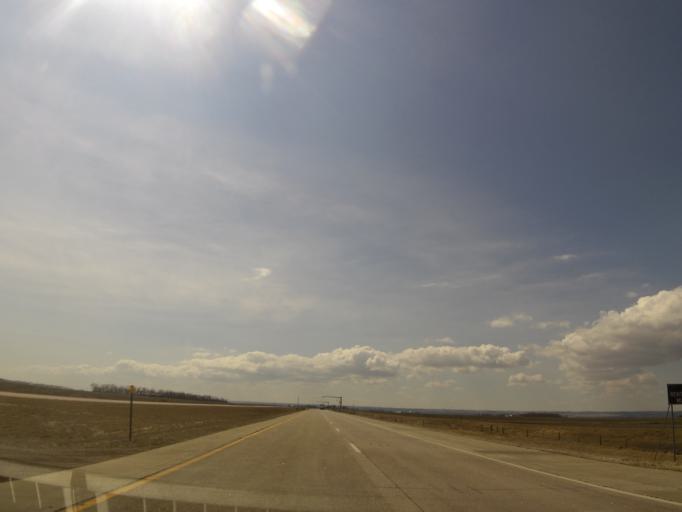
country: US
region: South Dakota
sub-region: Roberts County
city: Sisseton
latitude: 45.7120
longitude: -96.9565
